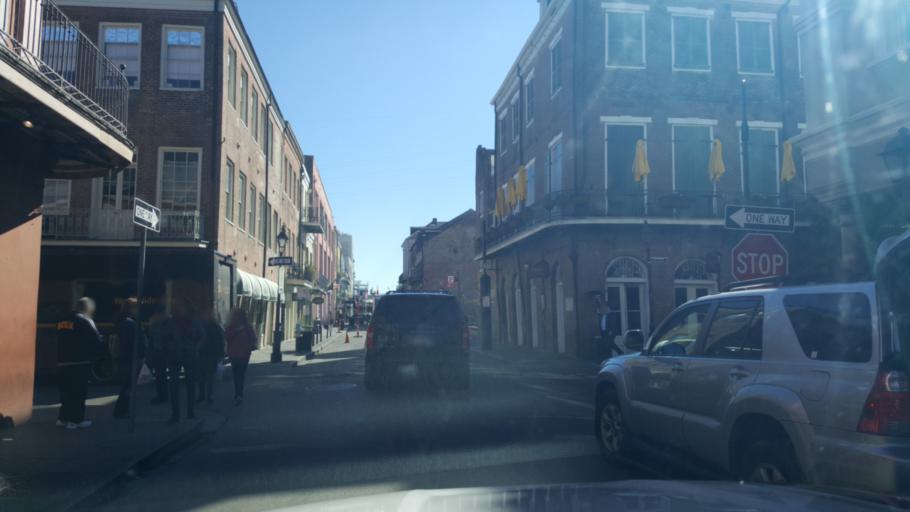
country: US
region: Louisiana
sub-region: Orleans Parish
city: New Orleans
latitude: 29.9567
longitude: -90.0648
